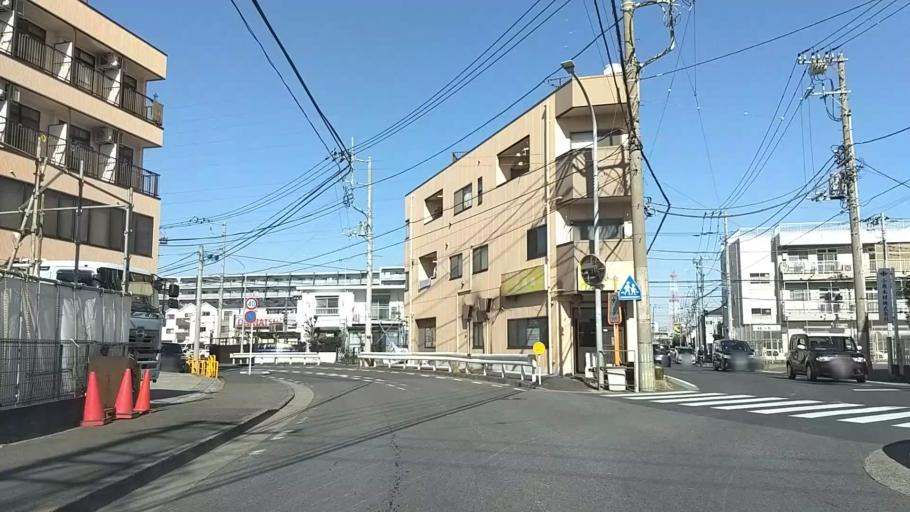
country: JP
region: Kanagawa
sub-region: Kawasaki-shi
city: Kawasaki
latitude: 35.5277
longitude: 139.6471
